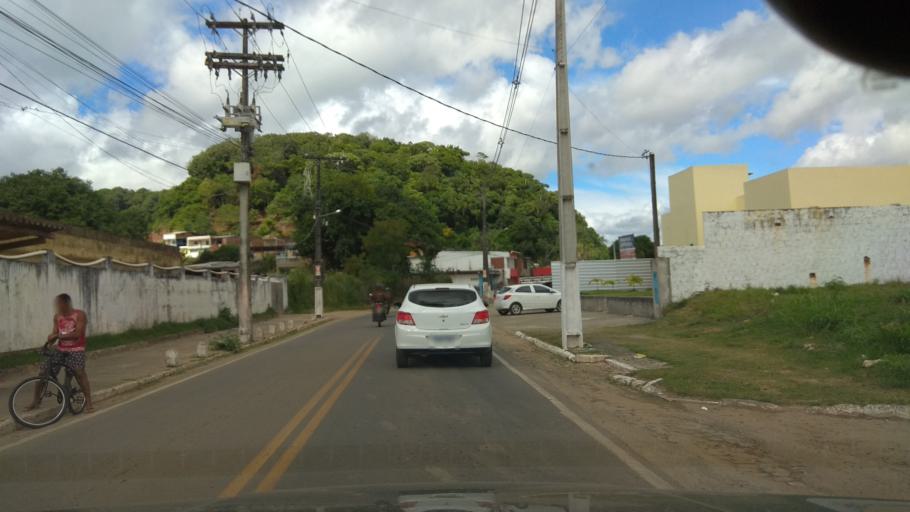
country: BR
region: Bahia
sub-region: Ilheus
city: Ilheus
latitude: -14.7890
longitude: -39.0606
